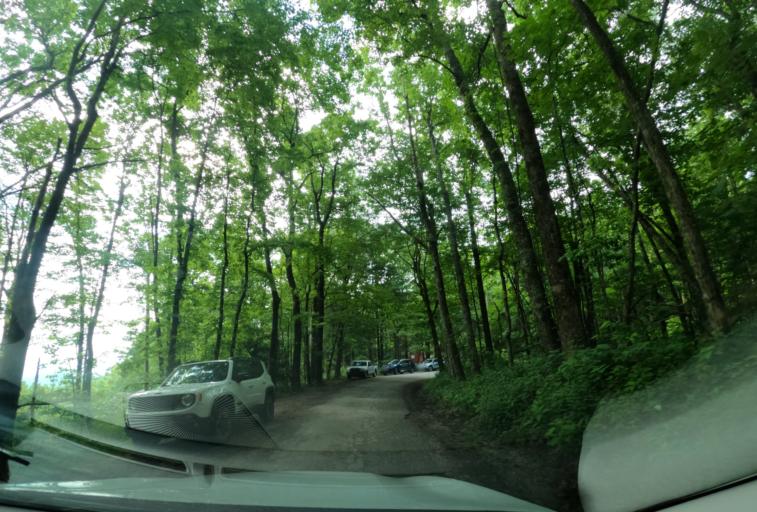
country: US
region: Georgia
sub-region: Rabun County
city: Mountain City
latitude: 34.9797
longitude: -83.3034
